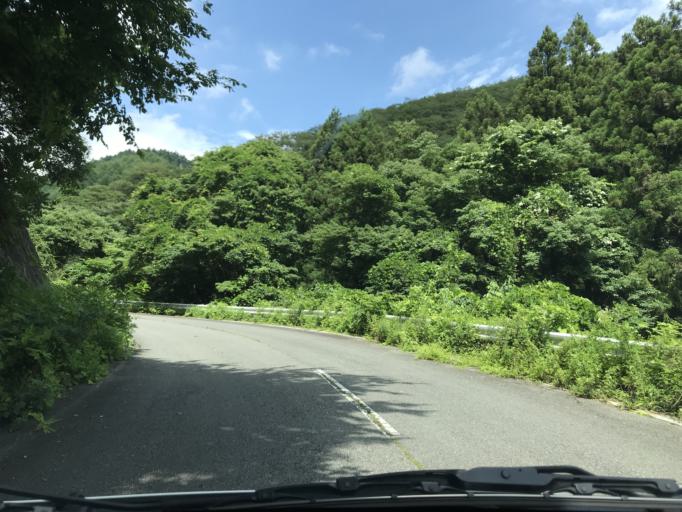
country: JP
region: Iwate
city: Tono
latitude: 39.0808
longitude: 141.4113
